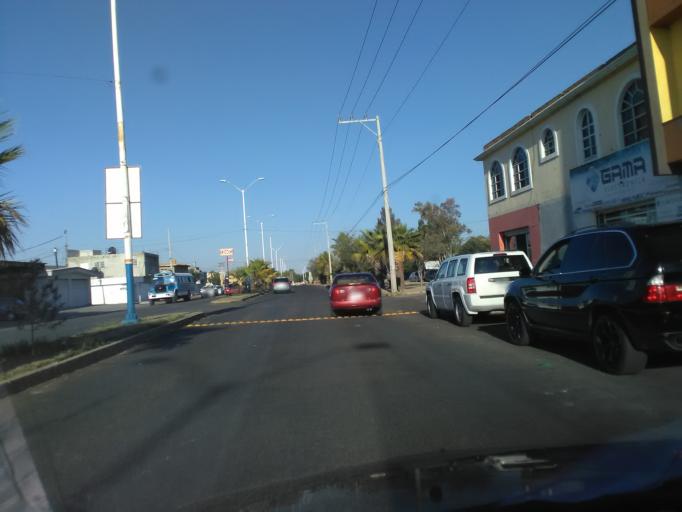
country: MX
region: Durango
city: Victoria de Durango
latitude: 24.0092
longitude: -104.6375
